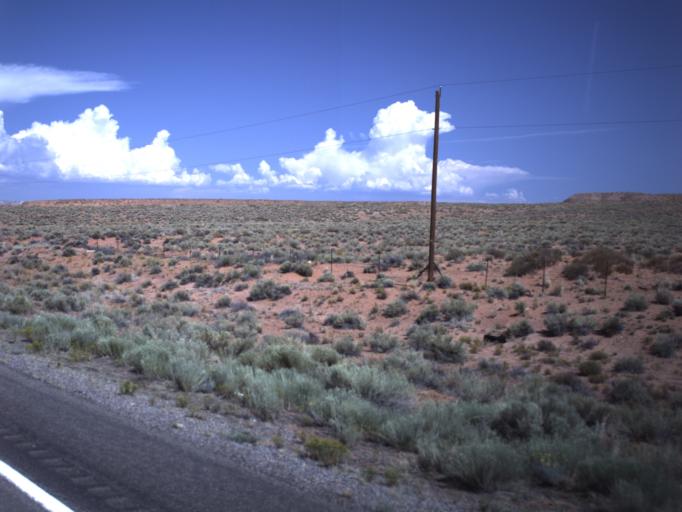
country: US
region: Utah
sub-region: San Juan County
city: Blanding
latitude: 37.1483
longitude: -109.5644
